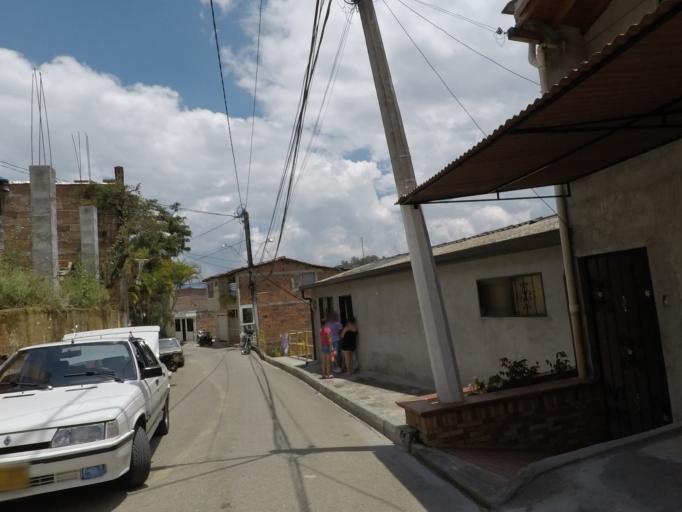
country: CO
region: Antioquia
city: Medellin
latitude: 6.2741
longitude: -75.6322
